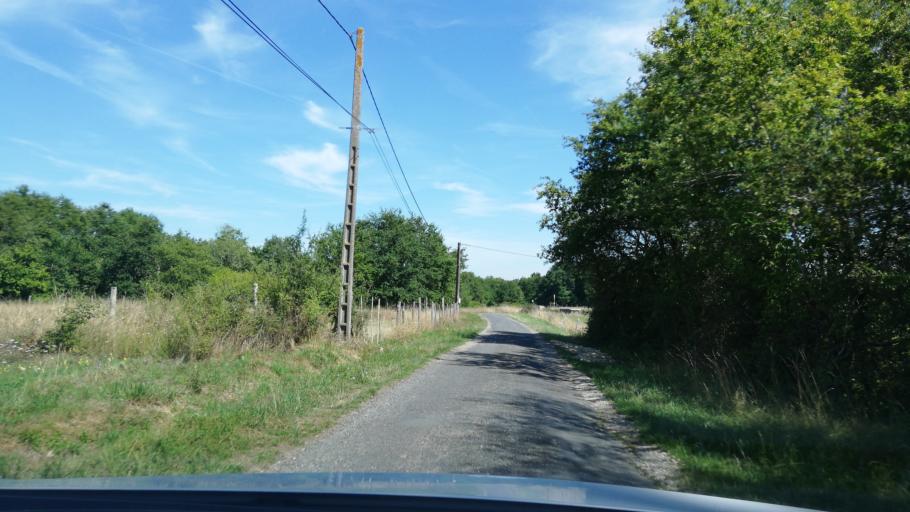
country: FR
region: Centre
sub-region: Departement d'Indre-et-Loire
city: Mazieres-de-Touraine
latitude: 47.3793
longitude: 0.4339
